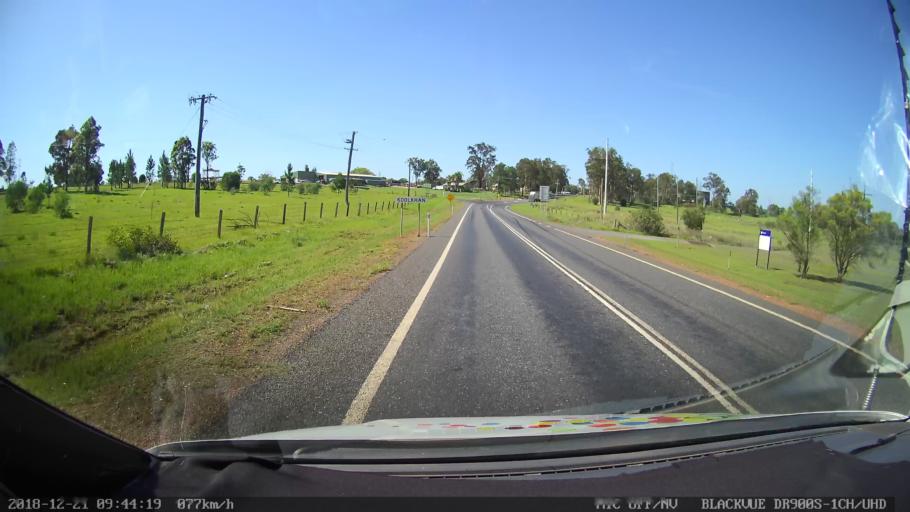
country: AU
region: New South Wales
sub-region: Clarence Valley
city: Grafton
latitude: -29.6168
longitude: 152.9340
